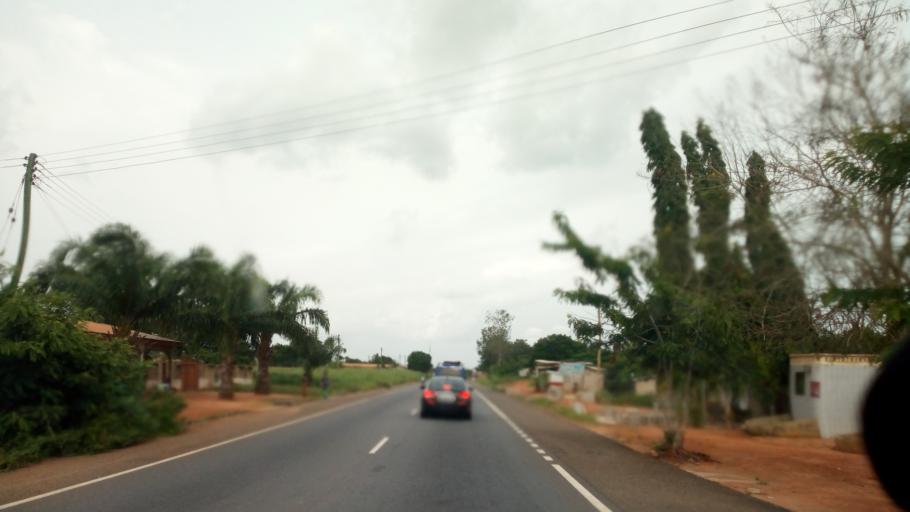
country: GH
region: Volta
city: Keta
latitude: 6.0645
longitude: 0.9047
